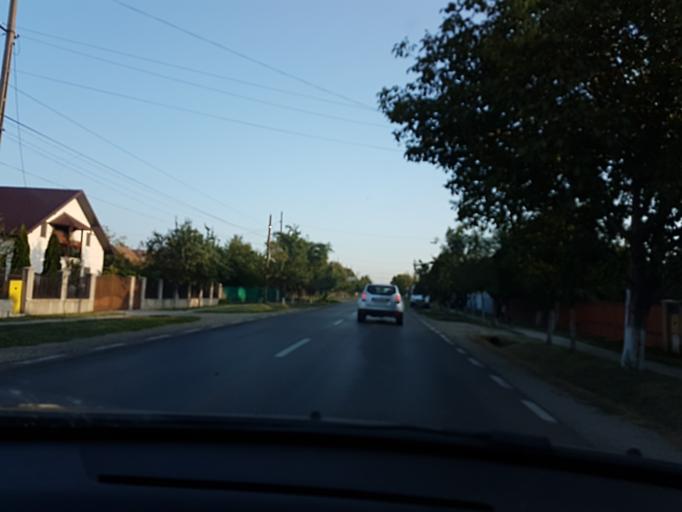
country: RO
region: Prahova
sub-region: Comuna Magurele
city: Magurele
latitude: 45.0907
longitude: 26.0368
